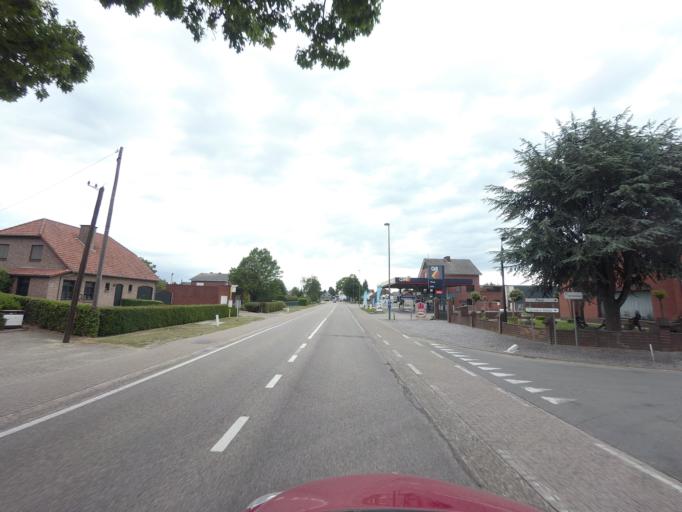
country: BE
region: Flanders
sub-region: Provincie Limburg
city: Lommel
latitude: 51.2021
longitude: 5.3056
